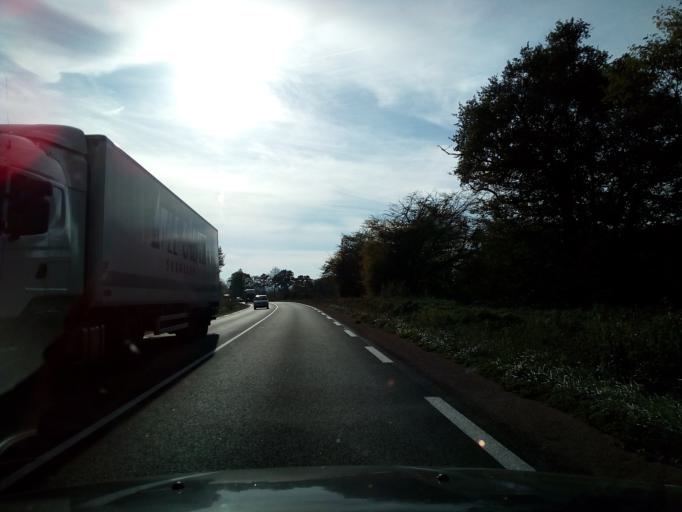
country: FR
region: Limousin
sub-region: Departement de la Haute-Vienne
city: Magnac-Laval
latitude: 46.1760
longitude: 1.1529
